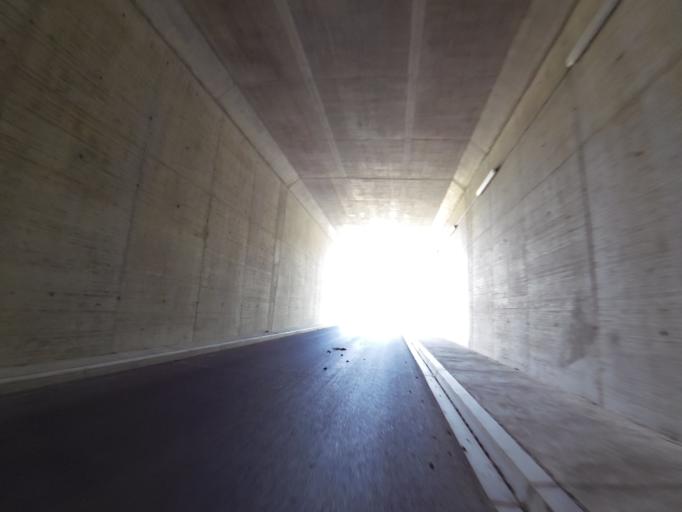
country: CH
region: Aargau
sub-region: Bezirk Rheinfelden
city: Rheinfelden
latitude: 47.5685
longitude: 7.8150
